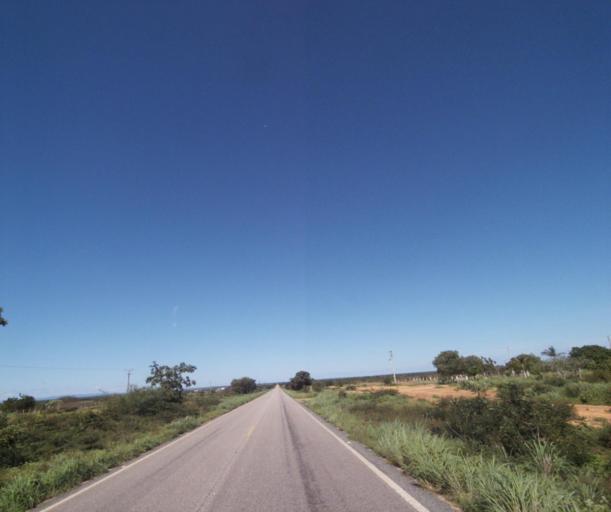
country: BR
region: Bahia
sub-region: Palmas De Monte Alto
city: Palmas de Monte Alto
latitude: -14.2561
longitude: -43.2440
